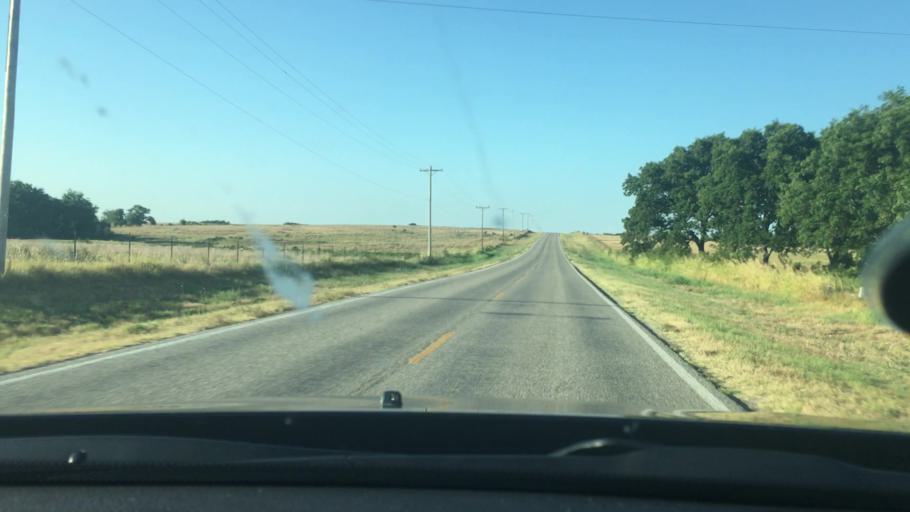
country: US
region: Oklahoma
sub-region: Murray County
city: Sulphur
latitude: 34.5880
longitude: -96.8449
